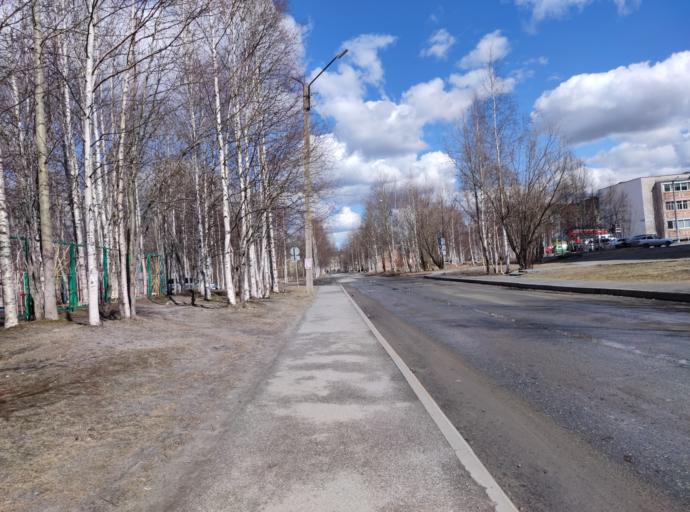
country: RU
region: Khanty-Mansiyskiy Avtonomnyy Okrug
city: Langepas
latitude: 61.2516
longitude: 75.1644
